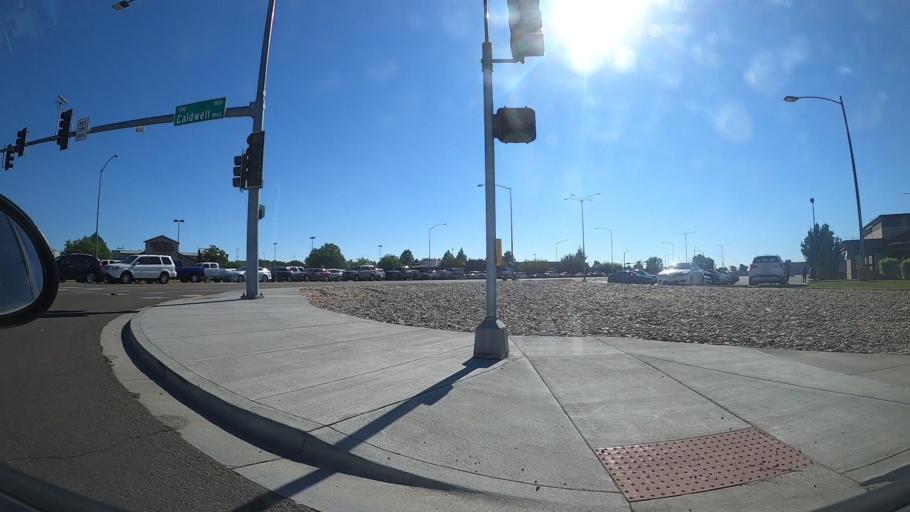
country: US
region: Idaho
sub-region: Canyon County
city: Nampa
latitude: 43.6066
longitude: -116.6049
